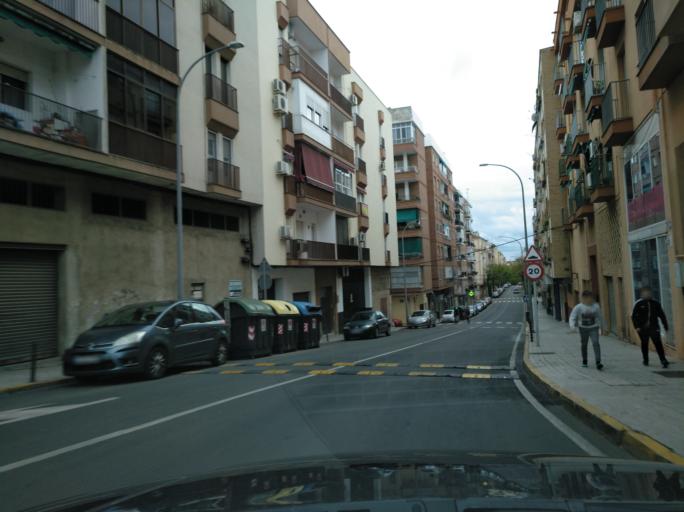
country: ES
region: Extremadura
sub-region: Provincia de Badajoz
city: Badajoz
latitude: 38.8889
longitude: -6.9759
